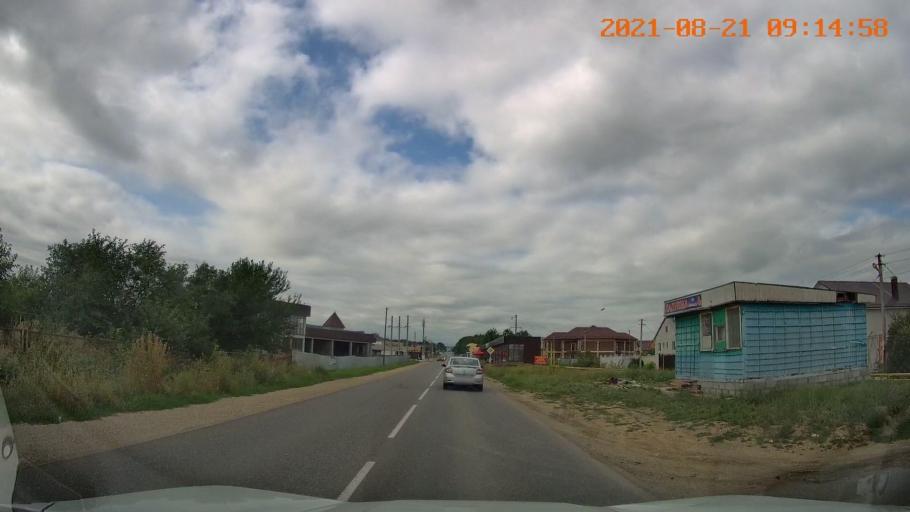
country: RU
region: Stavropol'skiy
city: Svobody
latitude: 43.9962
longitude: 43.0405
